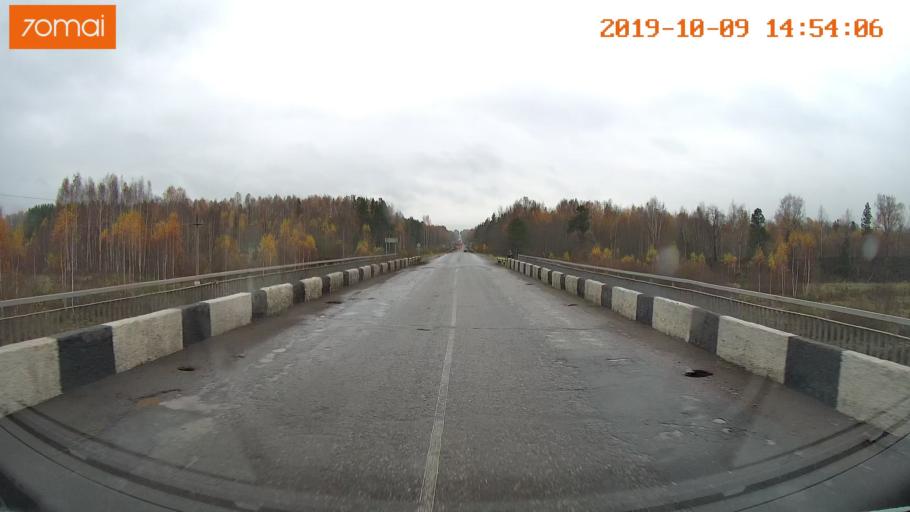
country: RU
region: Kostroma
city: Chistyye Bory
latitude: 58.3599
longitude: 41.6415
